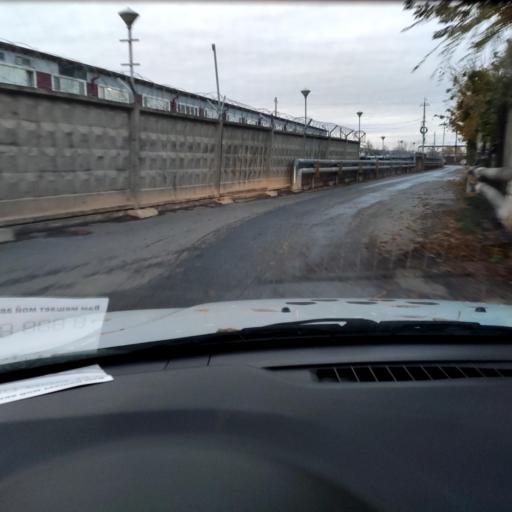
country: RU
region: Samara
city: Tol'yatti
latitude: 53.5475
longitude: 49.4371
